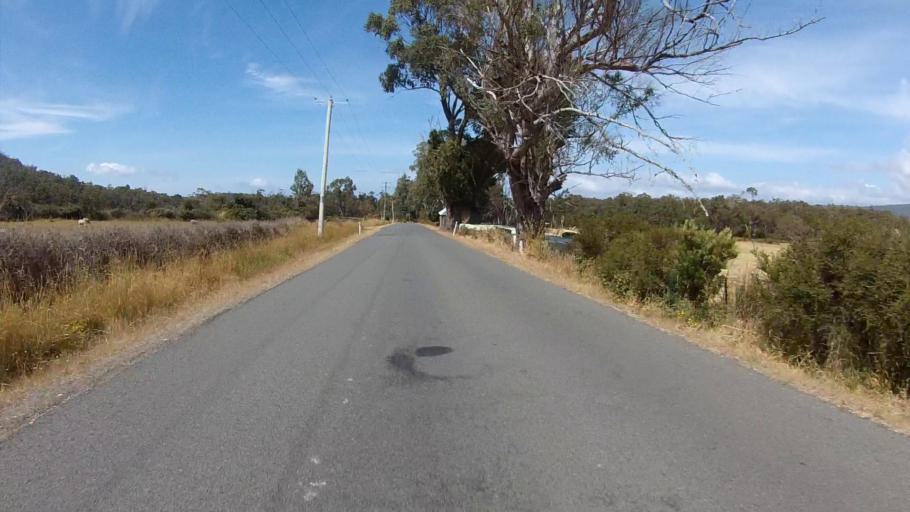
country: AU
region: Tasmania
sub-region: Huon Valley
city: Cygnet
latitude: -43.2368
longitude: 147.1251
